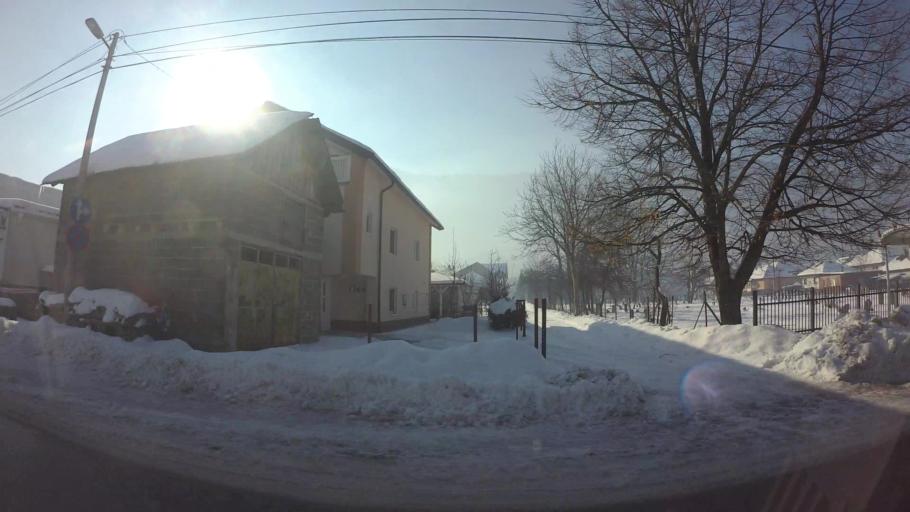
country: BA
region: Federation of Bosnia and Herzegovina
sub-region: Kanton Sarajevo
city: Sarajevo
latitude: 43.8041
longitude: 18.3043
